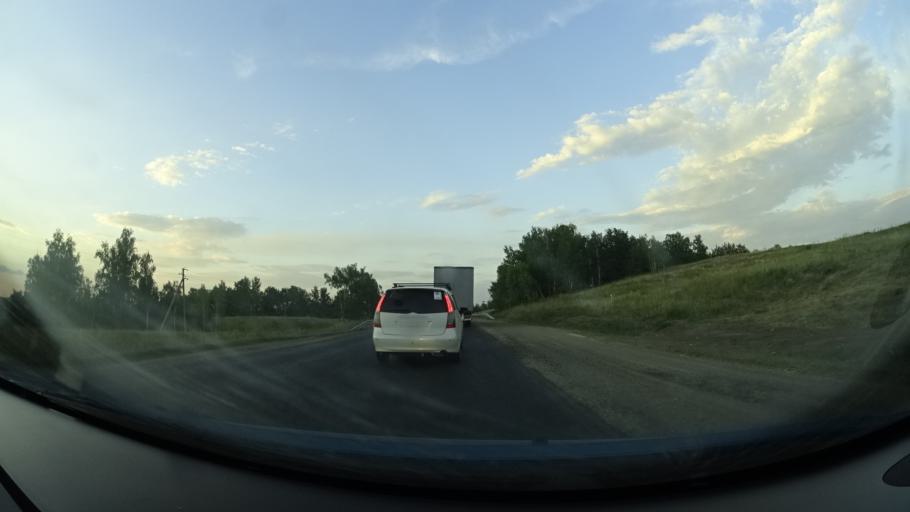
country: RU
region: Orenburg
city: Severnoye
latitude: 54.1487
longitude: 52.6144
